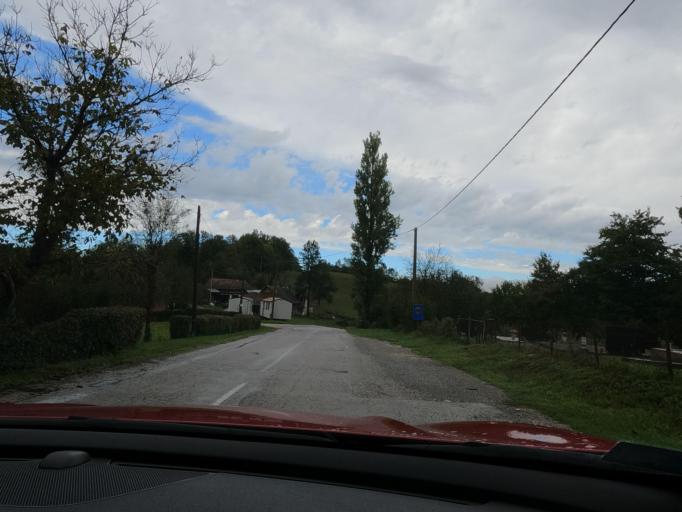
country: HR
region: Sisacko-Moslavacka
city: Glina
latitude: 45.3032
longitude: 16.1693
